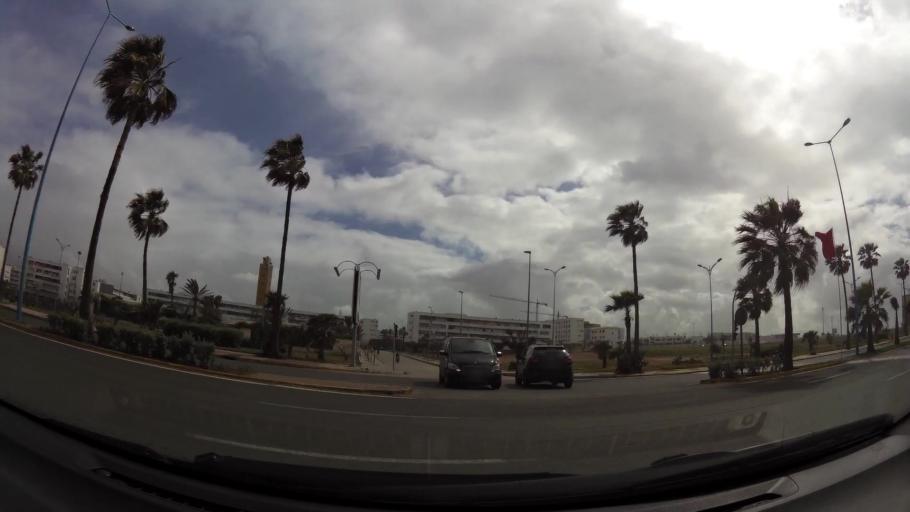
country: MA
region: Grand Casablanca
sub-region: Casablanca
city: Casablanca
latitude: 33.6070
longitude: -7.6527
